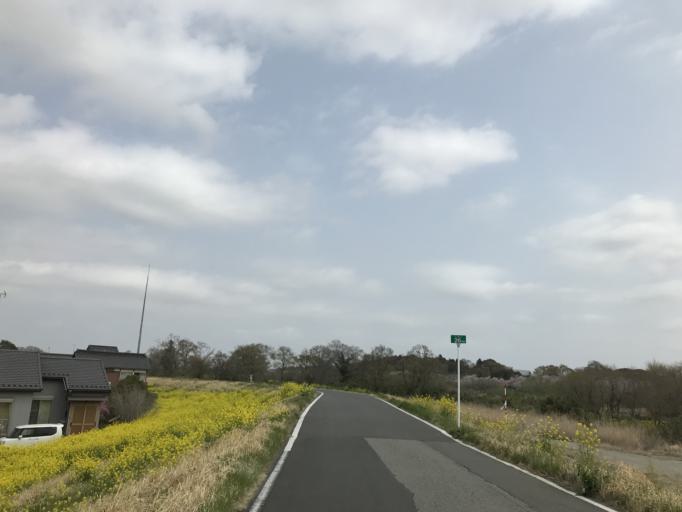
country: JP
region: Ibaraki
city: Mitsukaido
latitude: 36.0342
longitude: 140.0273
